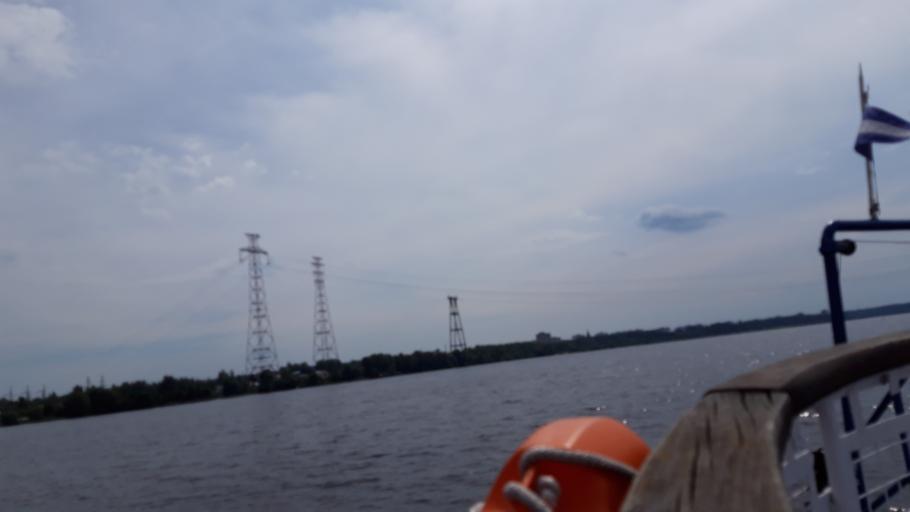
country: RU
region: Tverskaya
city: Konakovo
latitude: 56.7346
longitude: 36.7664
